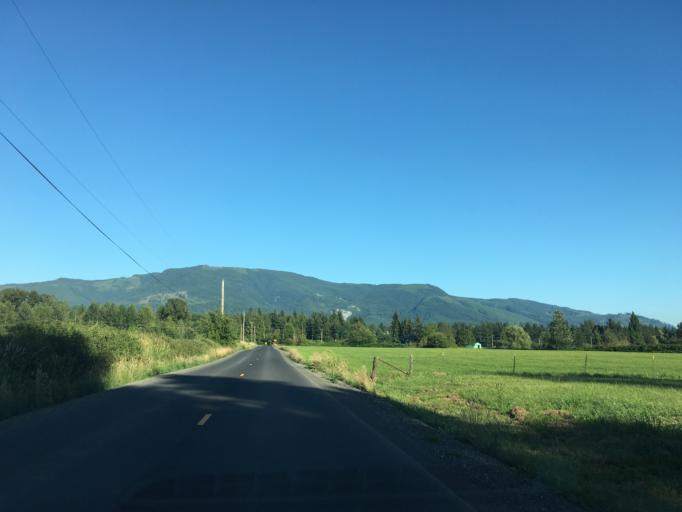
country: US
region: Washington
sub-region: Whatcom County
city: Nooksack
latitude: 48.9473
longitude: -122.3134
